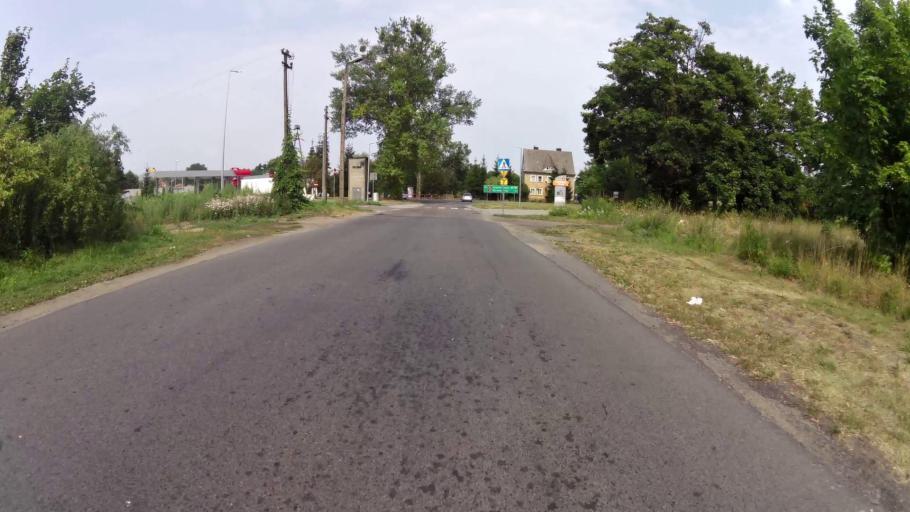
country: PL
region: West Pomeranian Voivodeship
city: Trzcinsko Zdroj
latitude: 52.9612
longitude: 14.6173
